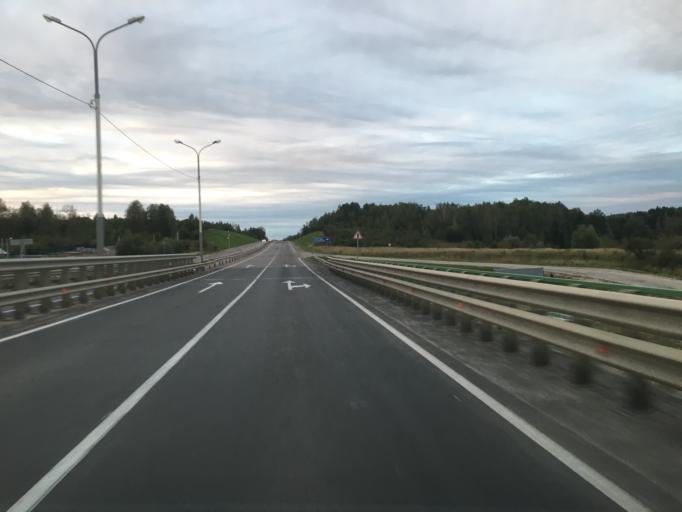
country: RU
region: Kaluga
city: Kaluga
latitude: 54.6005
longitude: 36.3199
